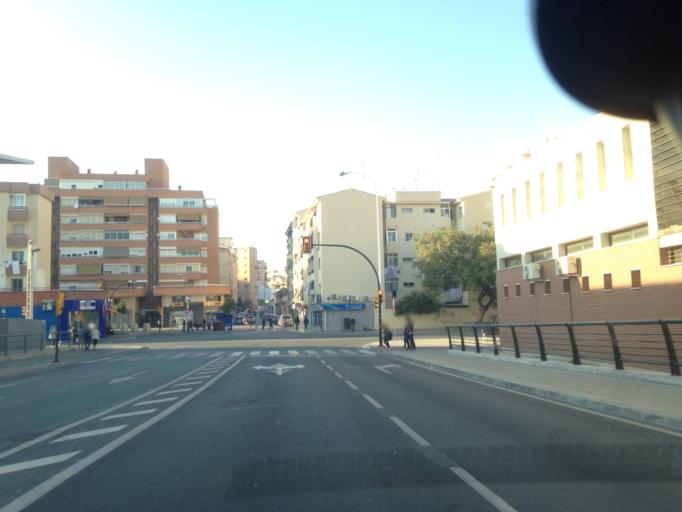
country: ES
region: Andalusia
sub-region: Provincia de Malaga
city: Malaga
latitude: 36.7107
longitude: -4.4381
